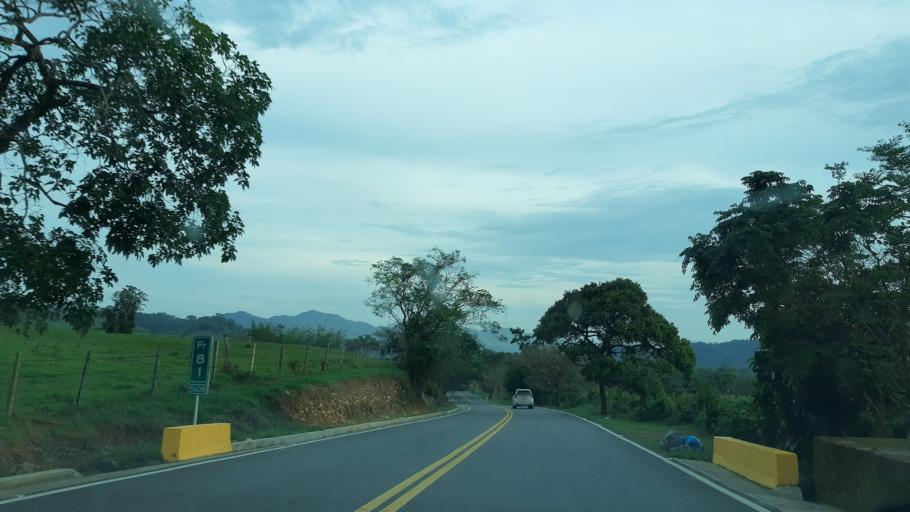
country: CO
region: Casanare
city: Sabanalarga
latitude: 4.8010
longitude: -73.0604
